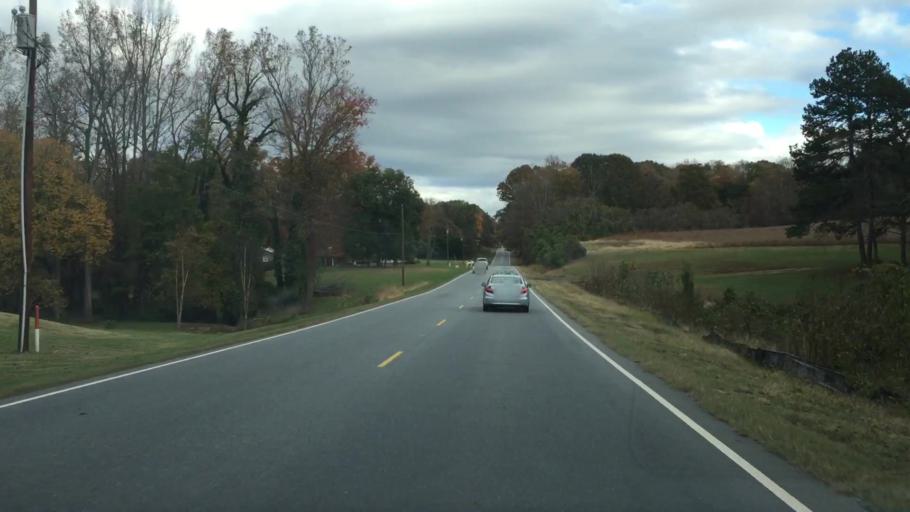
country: US
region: North Carolina
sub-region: Guilford County
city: Summerfield
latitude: 36.2643
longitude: -79.8588
